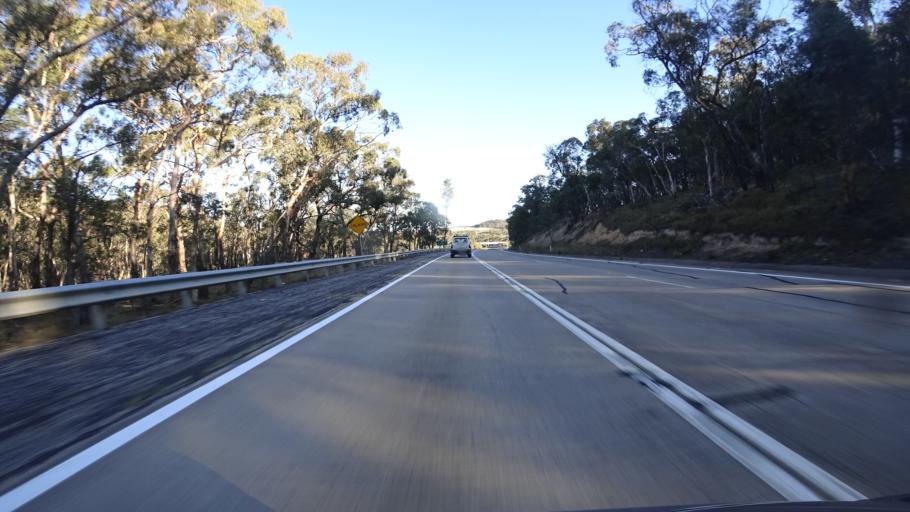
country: AU
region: New South Wales
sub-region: Lithgow
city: Portland
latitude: -33.3440
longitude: 150.0367
